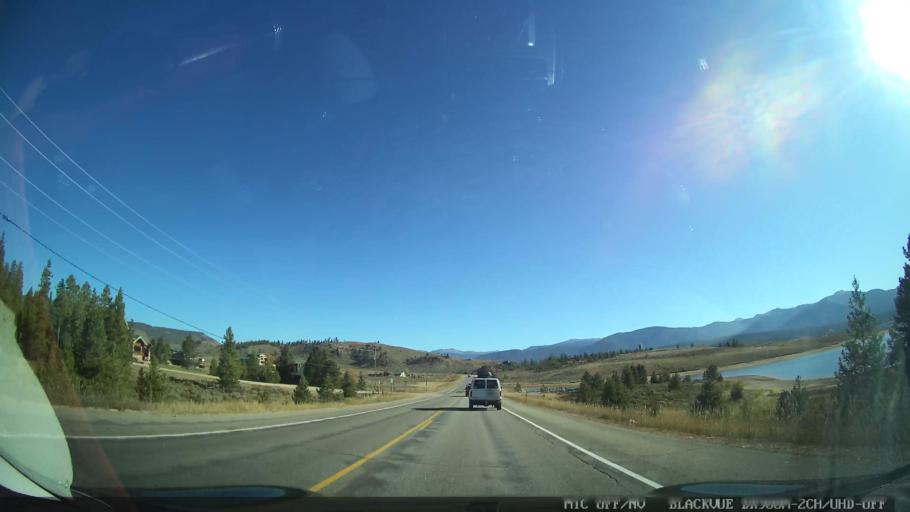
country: US
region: Colorado
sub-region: Grand County
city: Granby
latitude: 40.1780
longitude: -105.8965
